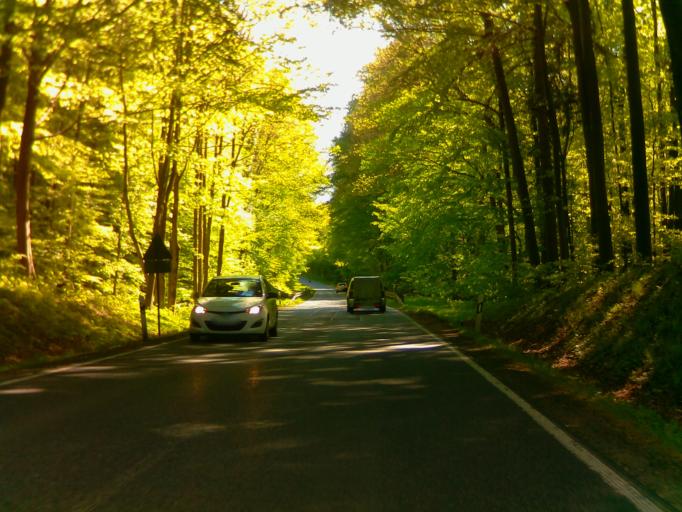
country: DE
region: Hesse
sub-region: Regierungsbezirk Darmstadt
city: Birstein
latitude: 50.3336
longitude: 9.2924
